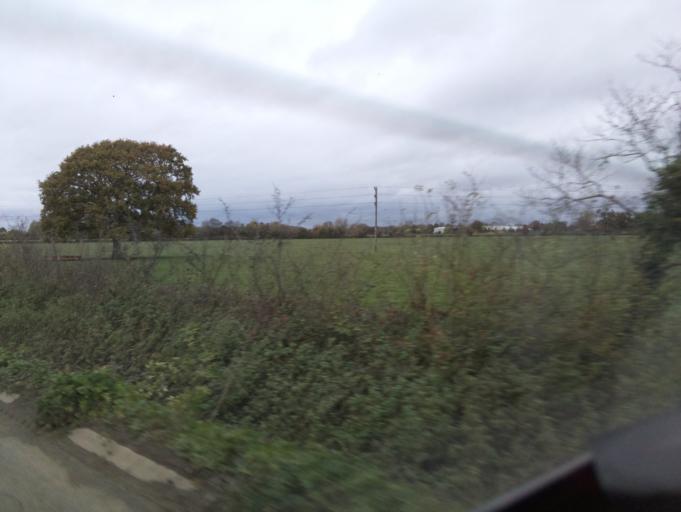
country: GB
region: England
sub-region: Dorset
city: Sherborne
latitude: 50.9925
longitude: -2.5768
